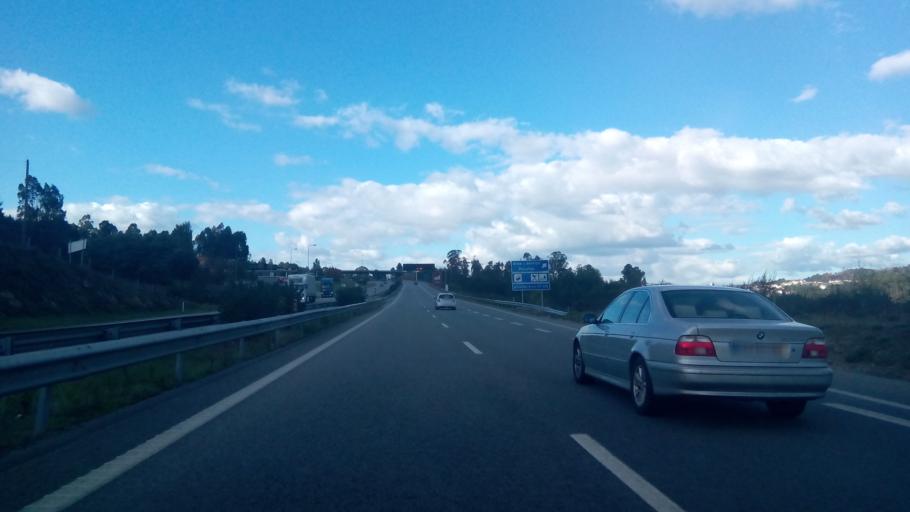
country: PT
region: Porto
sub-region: Marco de Canaveses
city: Marco de Canavezes
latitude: 41.2300
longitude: -8.1761
